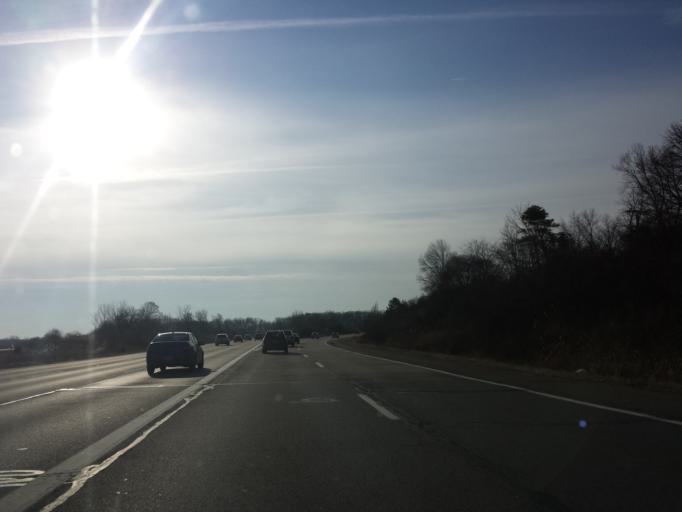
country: US
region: Michigan
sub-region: Oakland County
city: Bloomfield Hills
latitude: 42.6194
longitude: -83.2357
